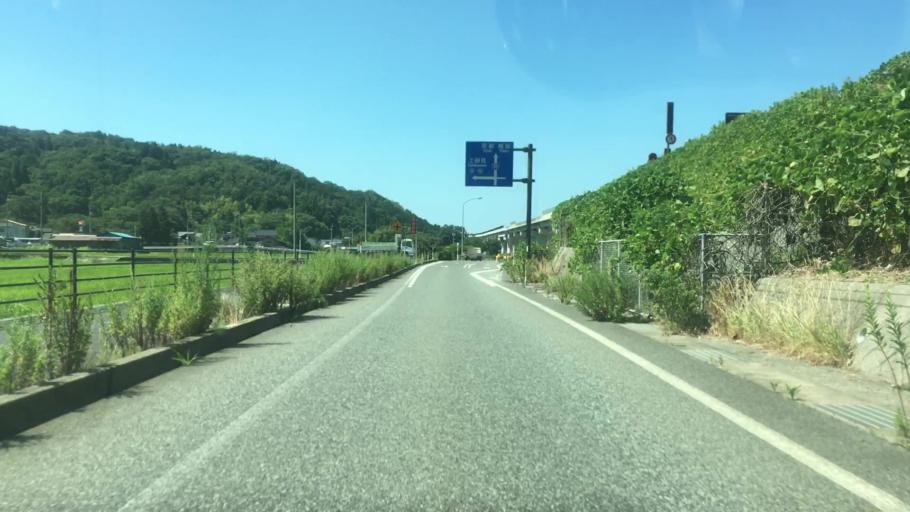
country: JP
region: Tottori
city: Tottori
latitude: 35.4330
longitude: 134.2048
